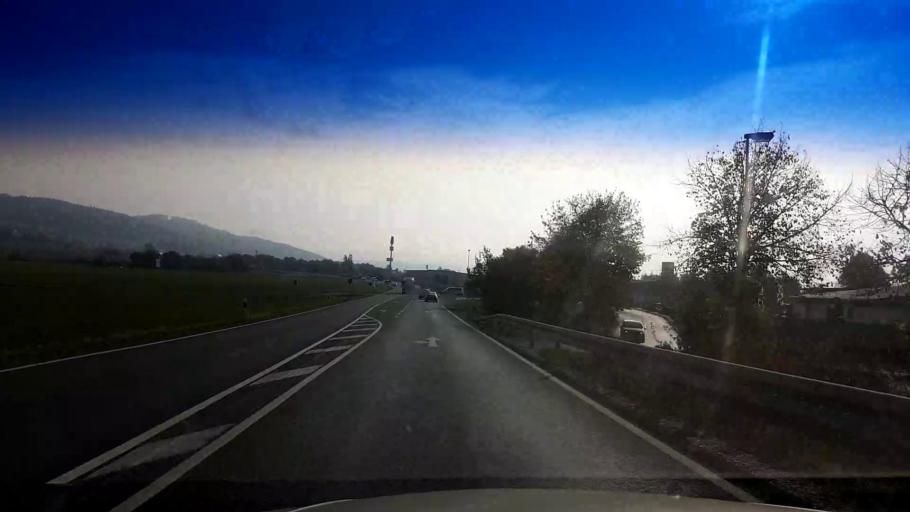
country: DE
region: Bavaria
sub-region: Upper Franconia
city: Himmelkron
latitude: 50.0569
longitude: 11.6108
